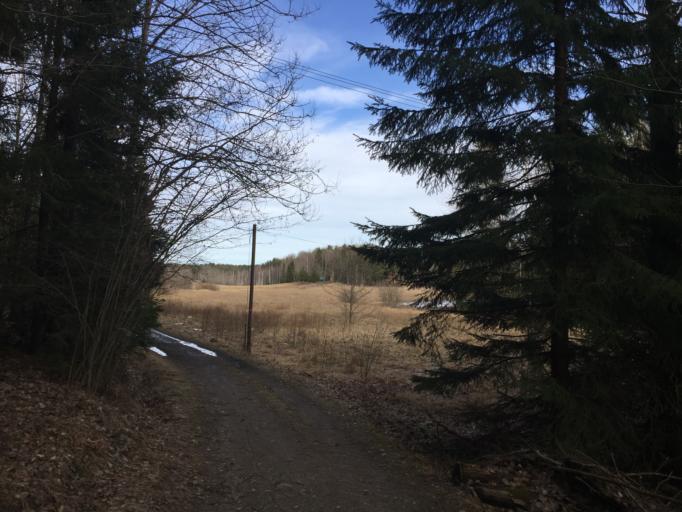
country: SE
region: Stockholm
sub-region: Botkyrka Kommun
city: Tullinge
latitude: 59.0956
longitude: 17.9658
